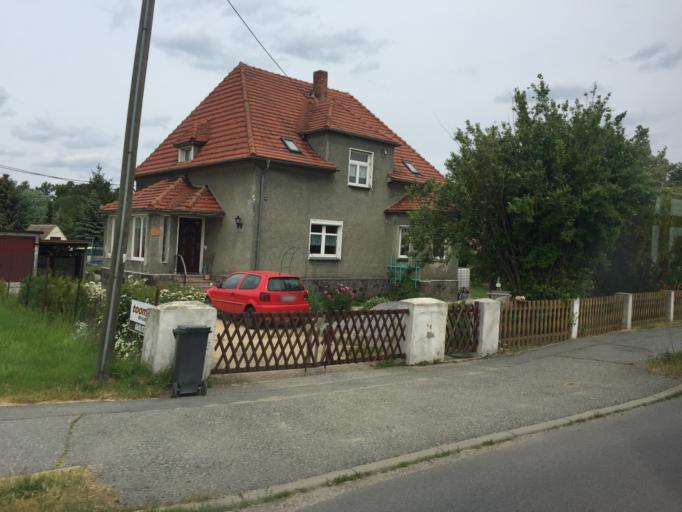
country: DE
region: Saxony
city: Markersdorf
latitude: 51.1472
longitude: 14.8929
